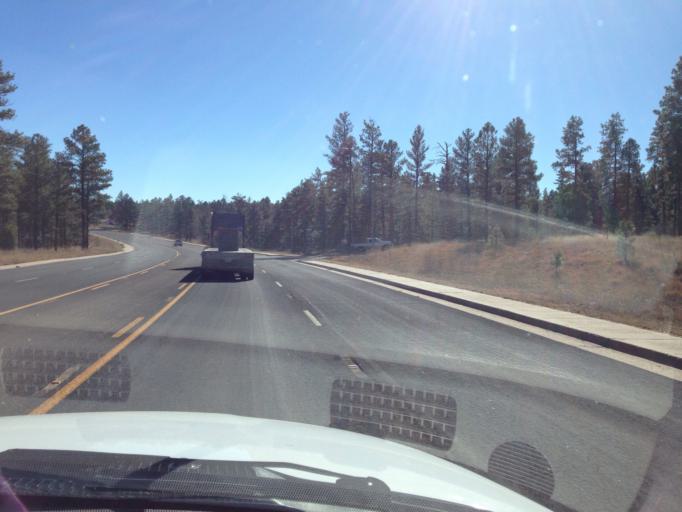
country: US
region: Arizona
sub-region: Navajo County
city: Show Low
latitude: 34.2466
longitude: -110.0708
